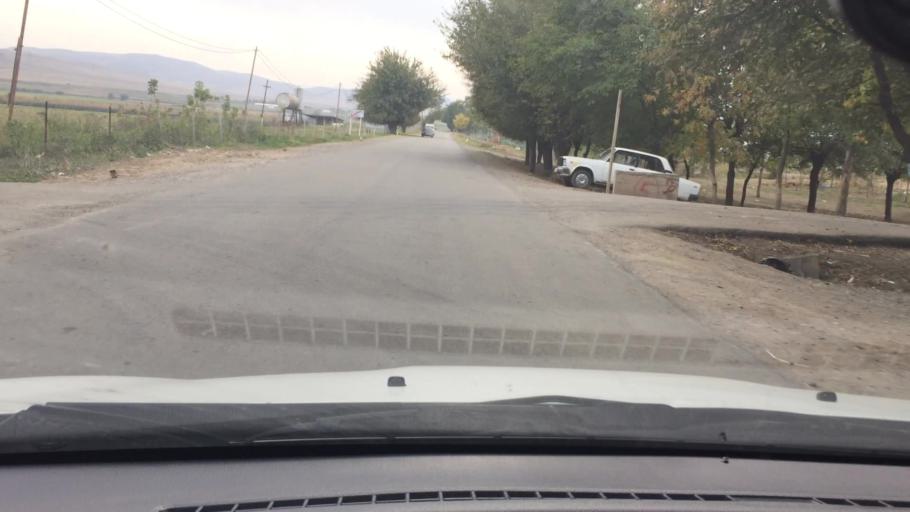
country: AM
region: Tavush
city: Berdavan
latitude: 41.3531
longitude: 44.9631
